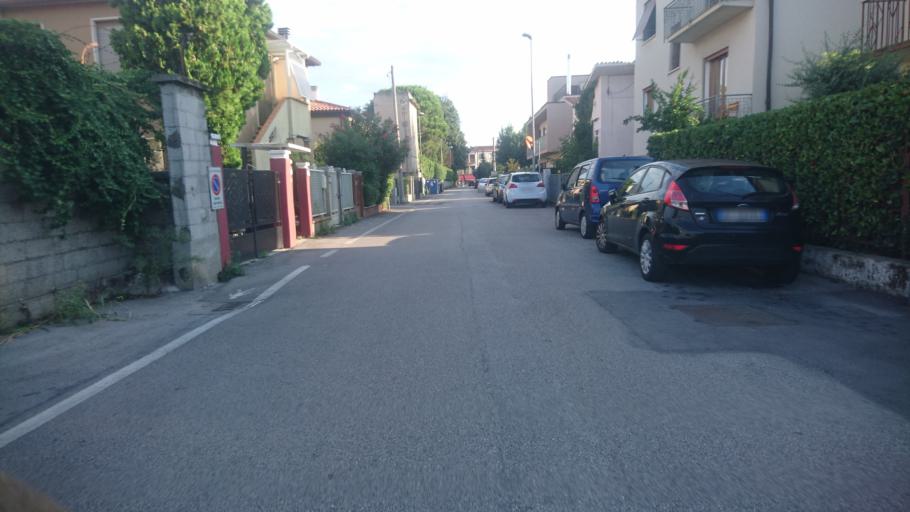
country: IT
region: Veneto
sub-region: Provincia di Padova
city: Mandriola-Sant'Agostino
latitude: 45.3992
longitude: 11.8561
